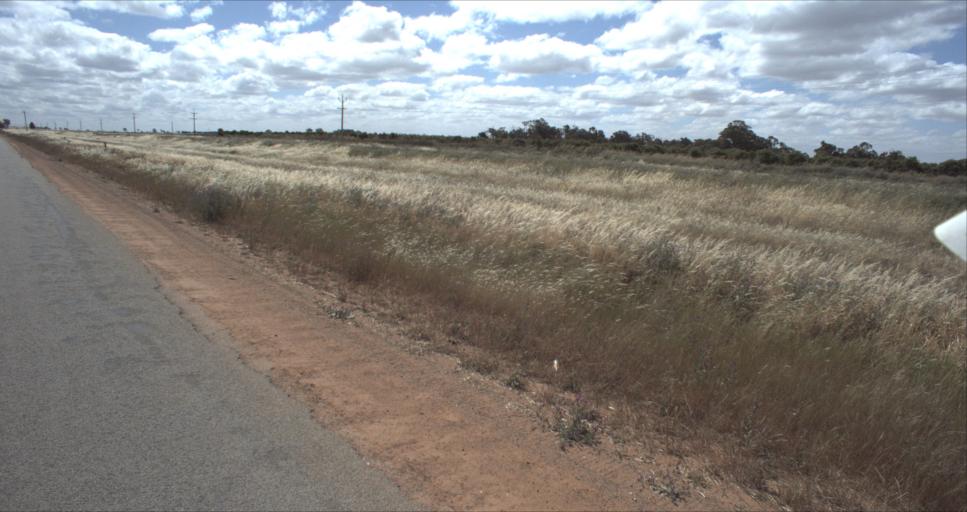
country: AU
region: New South Wales
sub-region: Leeton
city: Leeton
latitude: -34.5897
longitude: 146.3674
